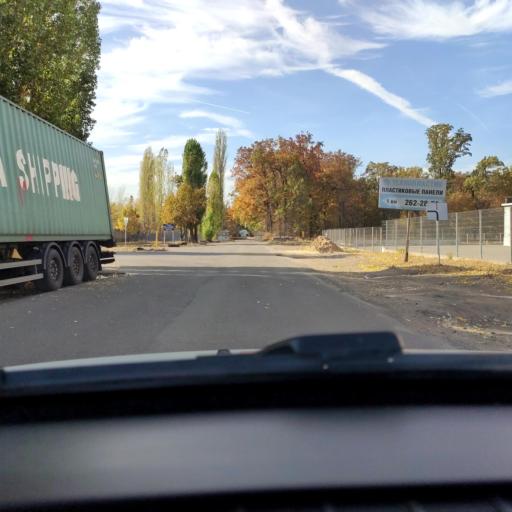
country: RU
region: Voronezj
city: Podgornoye
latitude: 51.8074
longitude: 39.2010
